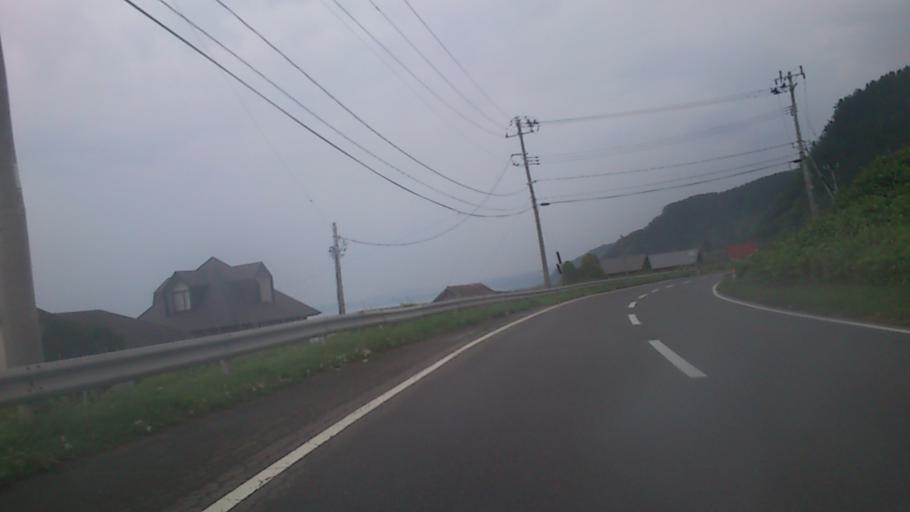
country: JP
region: Akita
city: Noshiromachi
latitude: 40.4572
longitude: 139.9429
